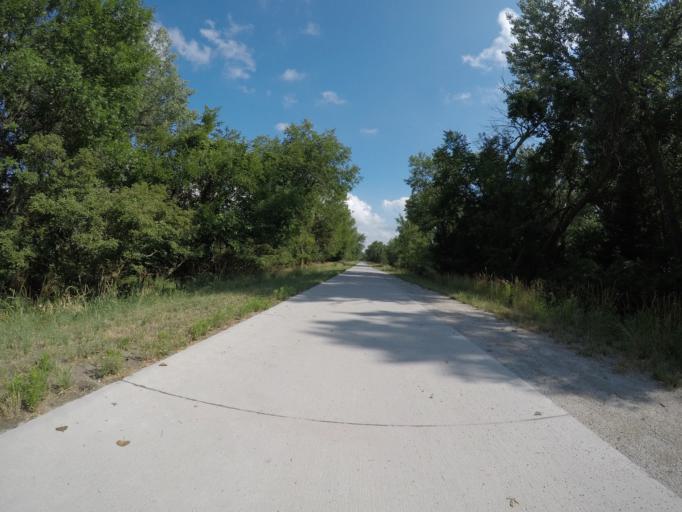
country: US
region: Nebraska
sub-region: Buffalo County
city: Kearney
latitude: 40.6596
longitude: -98.9871
